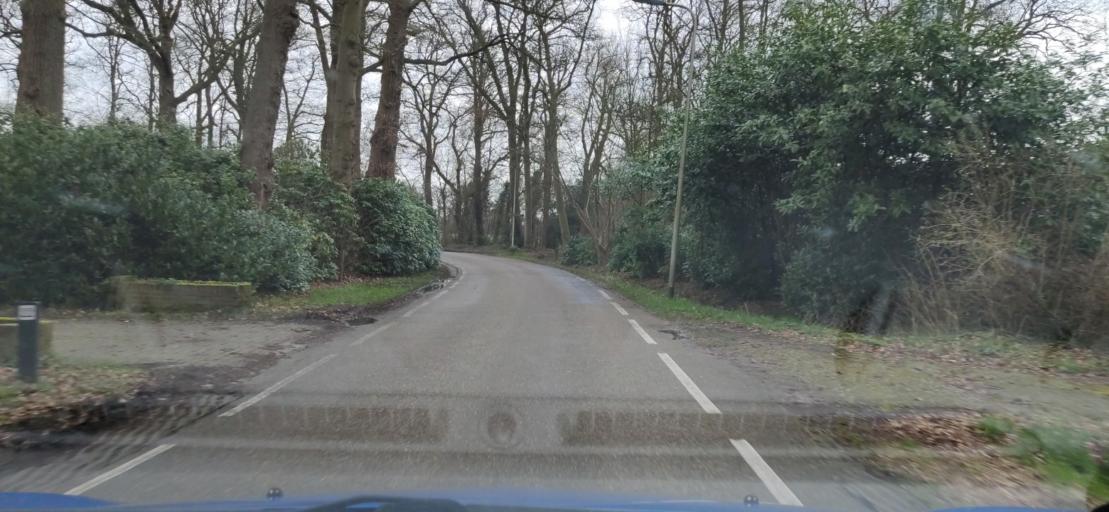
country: NL
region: Overijssel
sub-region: Gemeente Hengelo
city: Hengelo
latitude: 52.2100
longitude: 6.7805
